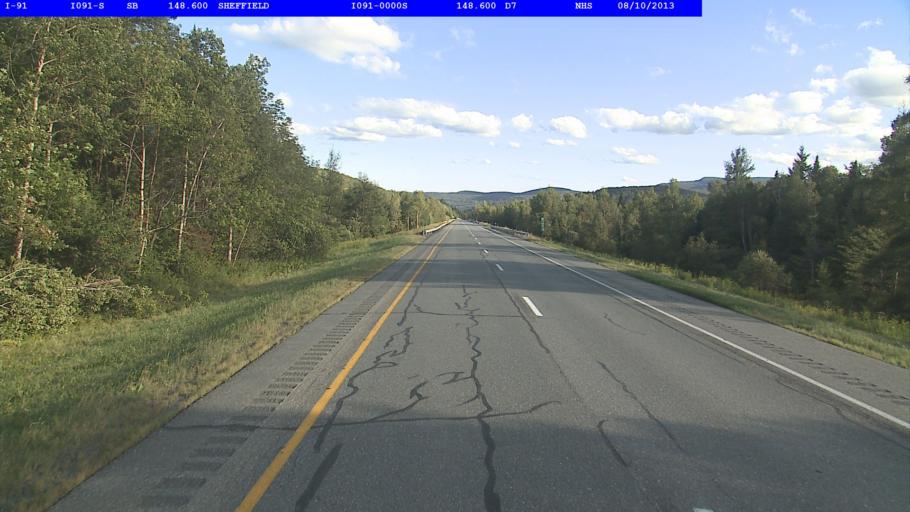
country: US
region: Vermont
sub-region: Caledonia County
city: Lyndonville
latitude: 44.6445
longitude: -72.1327
